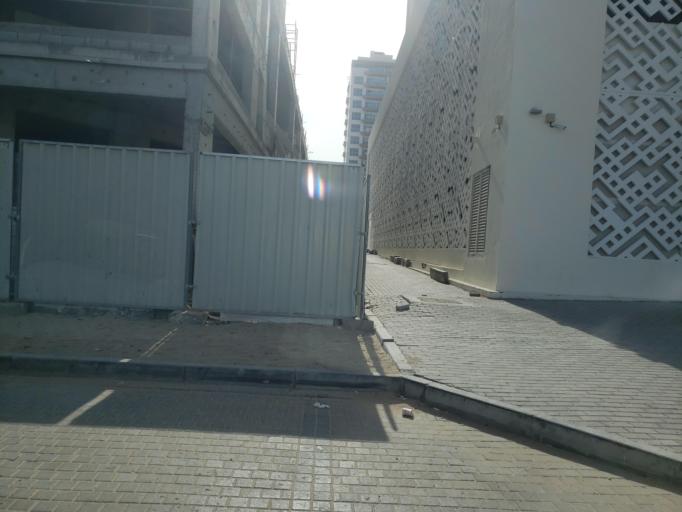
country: AE
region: Dubai
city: Dubai
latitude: 25.0304
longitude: 55.1406
